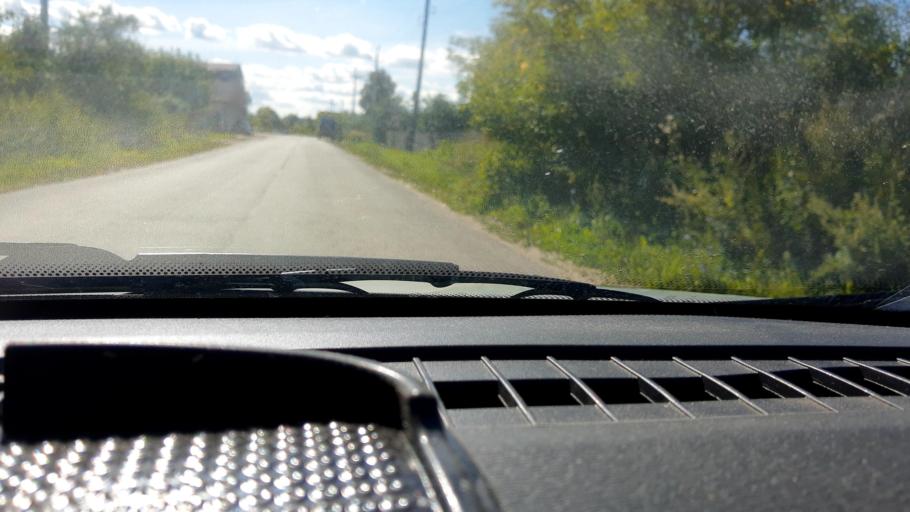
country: RU
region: Nizjnij Novgorod
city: Lukino
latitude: 56.4368
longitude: 43.6659
